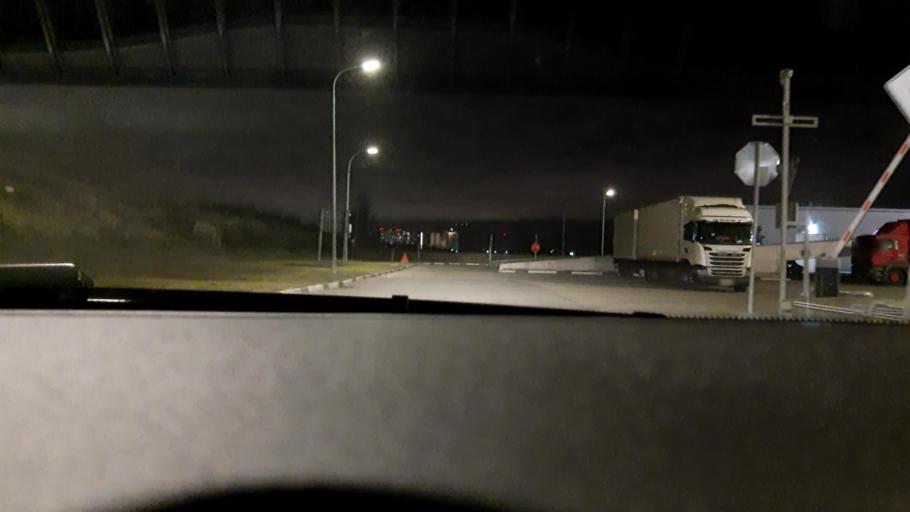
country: RU
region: Nizjnij Novgorod
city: Afonino
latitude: 56.2264
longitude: 44.0672
